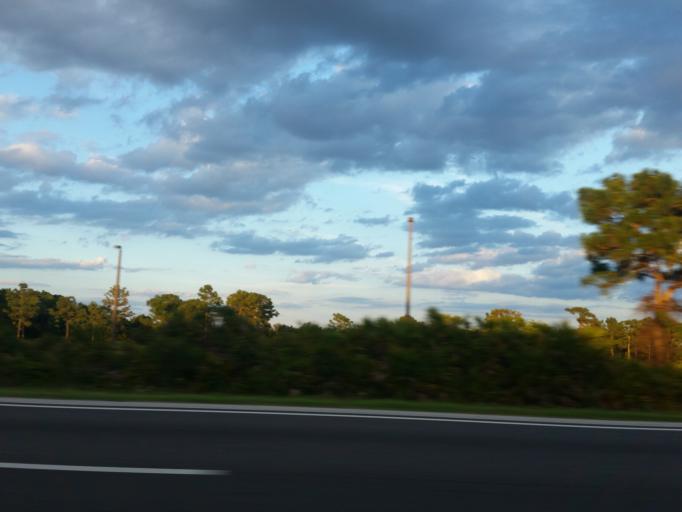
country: US
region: Florida
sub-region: Sarasota County
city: The Meadows
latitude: 27.3759
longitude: -82.4458
